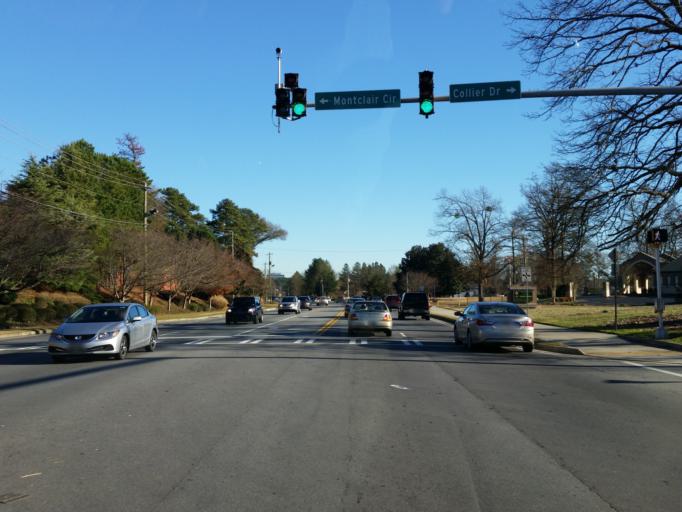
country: US
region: Georgia
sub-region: Cobb County
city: Smyrna
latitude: 33.8776
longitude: -84.5087
